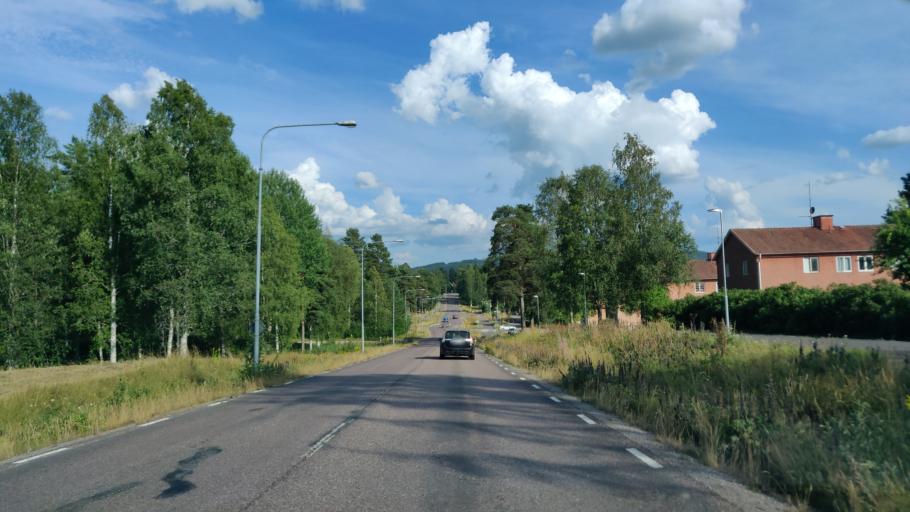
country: SE
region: Vaermland
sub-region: Hagfors Kommun
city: Hagfors
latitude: 60.0459
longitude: 13.6770
